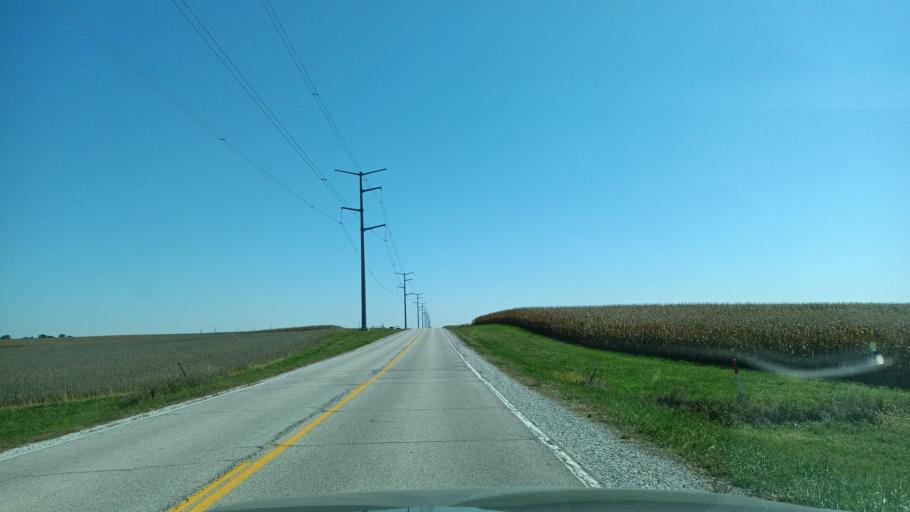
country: US
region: Illinois
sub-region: Peoria County
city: Elmwood
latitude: 40.9023
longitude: -90.0023
